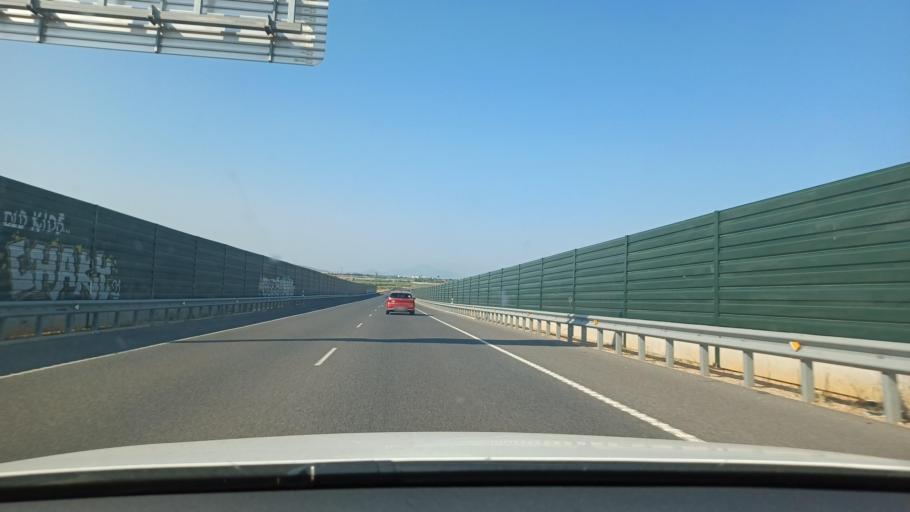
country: ES
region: Valencia
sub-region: Provincia de Castello
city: Benicarlo
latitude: 40.4141
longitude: 0.3837
